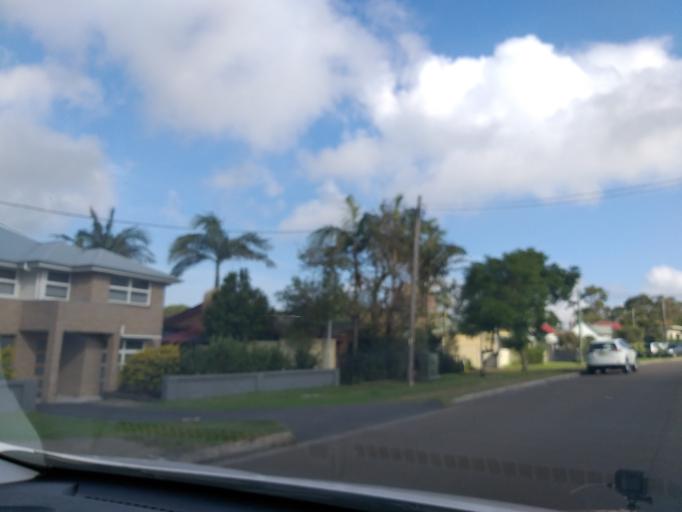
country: AU
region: New South Wales
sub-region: Wollongong
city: Helensburgh
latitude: -34.1930
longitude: 150.9770
